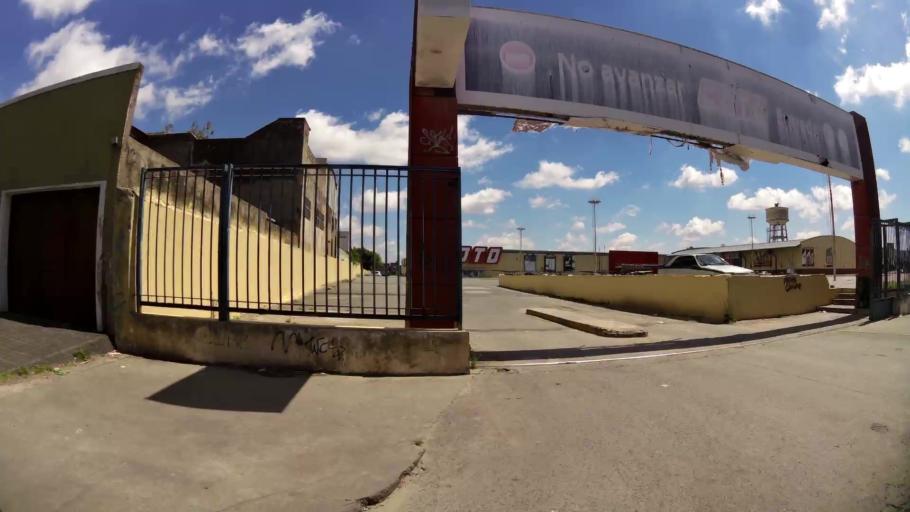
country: AR
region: Buenos Aires
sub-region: Partido de Lanus
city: Lanus
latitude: -34.6932
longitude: -58.4196
